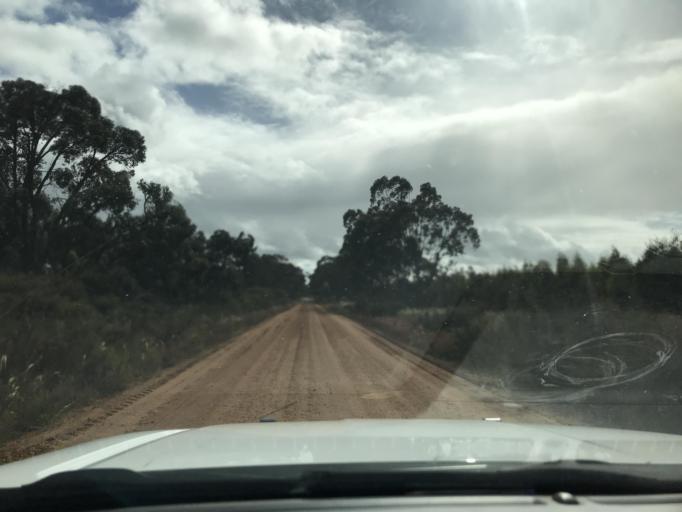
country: AU
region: South Australia
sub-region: Wattle Range
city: Penola
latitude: -37.1876
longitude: 141.1929
